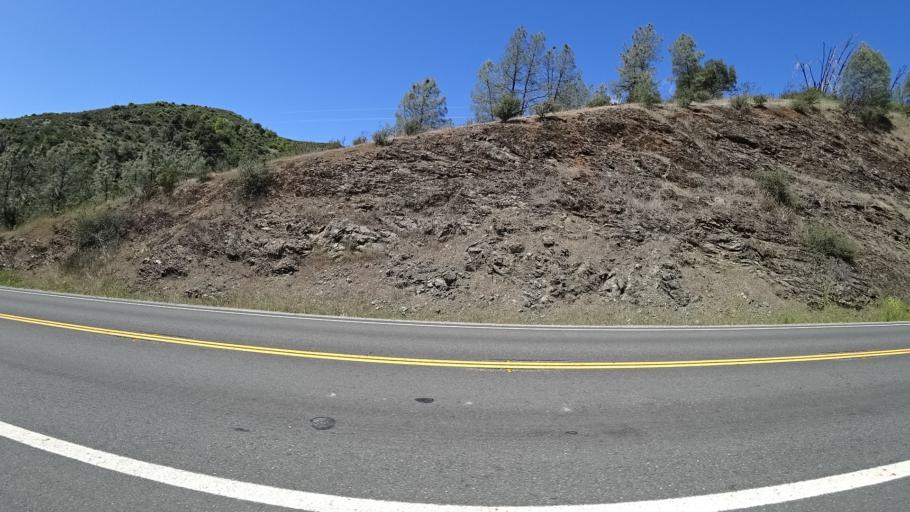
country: US
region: California
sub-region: Trinity County
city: Weaverville
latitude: 40.7331
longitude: -123.0194
